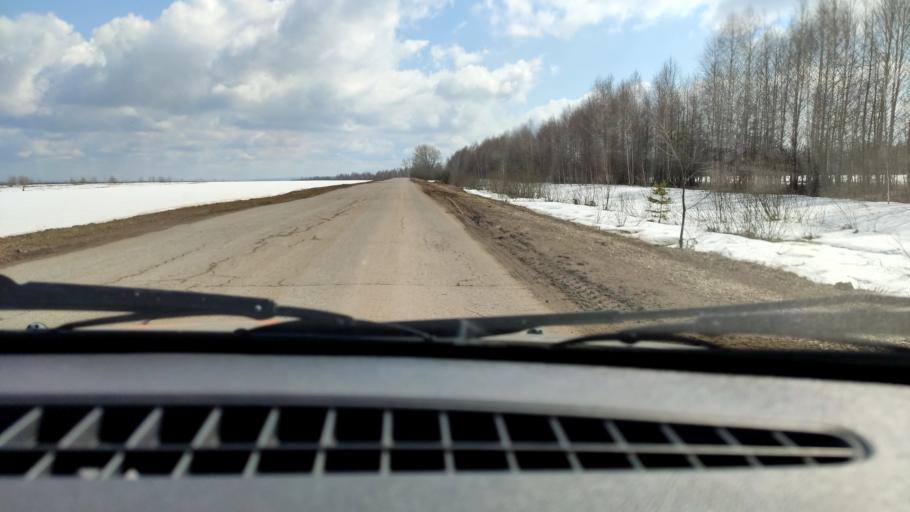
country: RU
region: Bashkortostan
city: Kudeyevskiy
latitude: 54.8646
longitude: 56.7492
